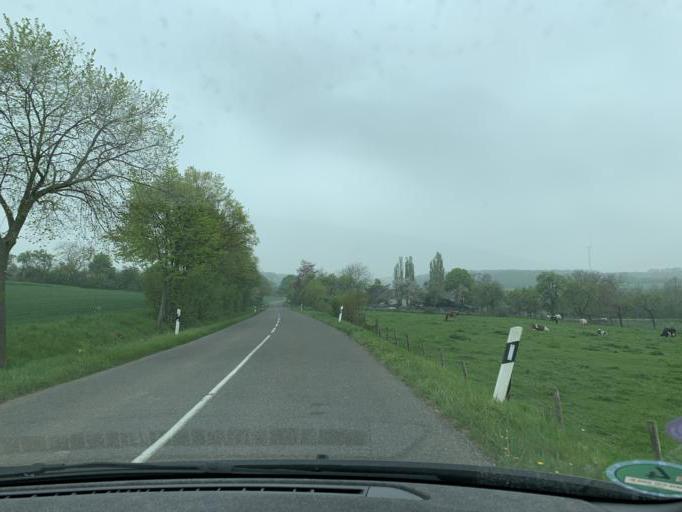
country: DE
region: North Rhine-Westphalia
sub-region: Regierungsbezirk Koln
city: Nideggen
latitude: 50.6910
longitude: 6.5339
